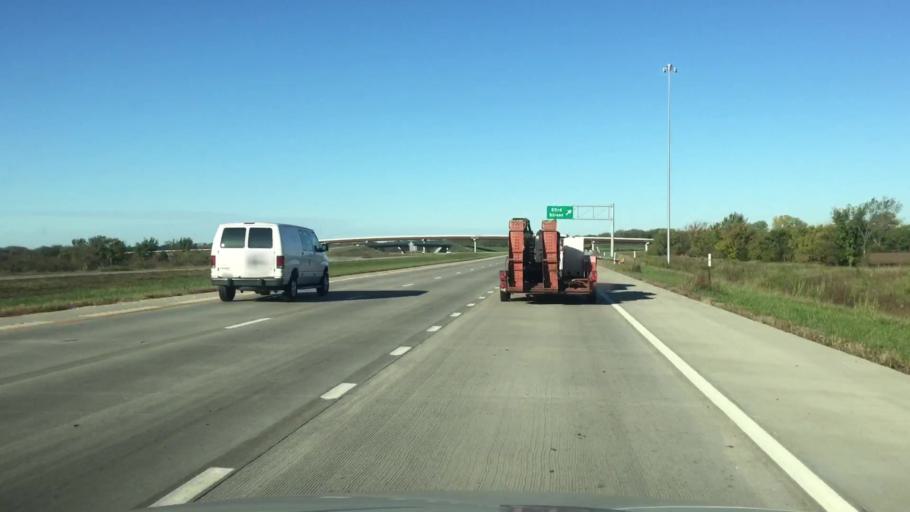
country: US
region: Kansas
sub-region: Douglas County
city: Eudora
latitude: 38.9358
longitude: -95.1621
